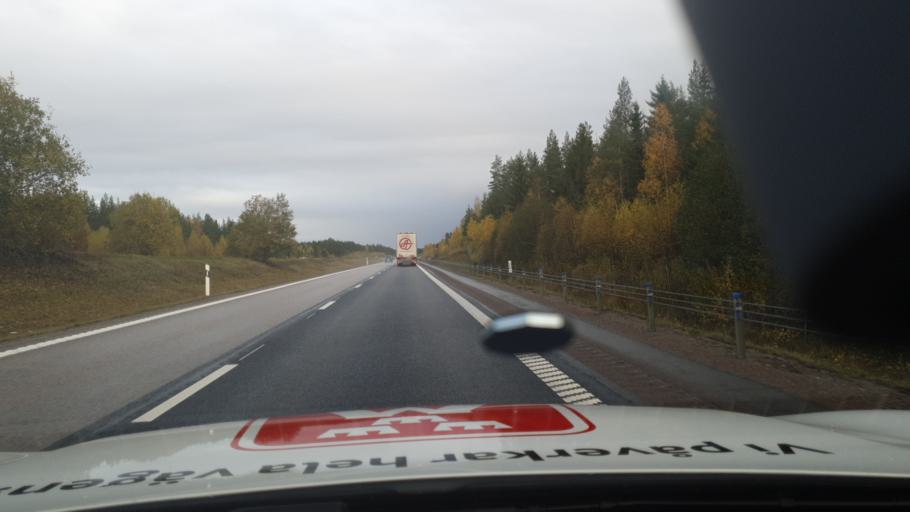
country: SE
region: Uppsala
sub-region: Tierps Kommun
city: Tierp
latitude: 60.2442
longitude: 17.5018
